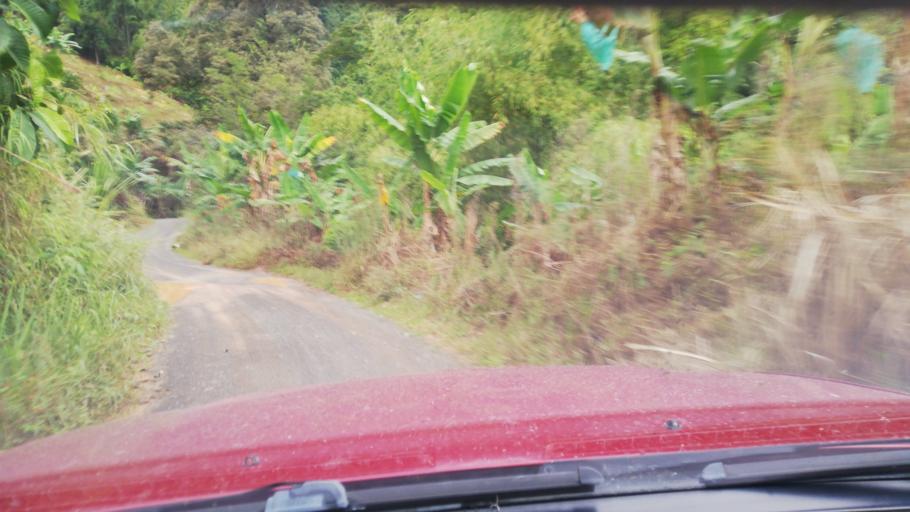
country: CO
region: Risaralda
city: Balboa
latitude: 4.8872
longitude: -75.9678
